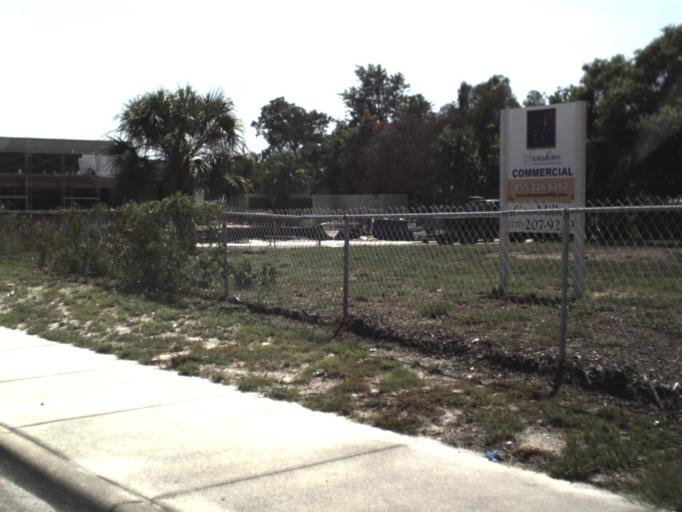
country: US
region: Florida
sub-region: Pinellas County
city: Clearwater
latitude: 27.9785
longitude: -82.7960
